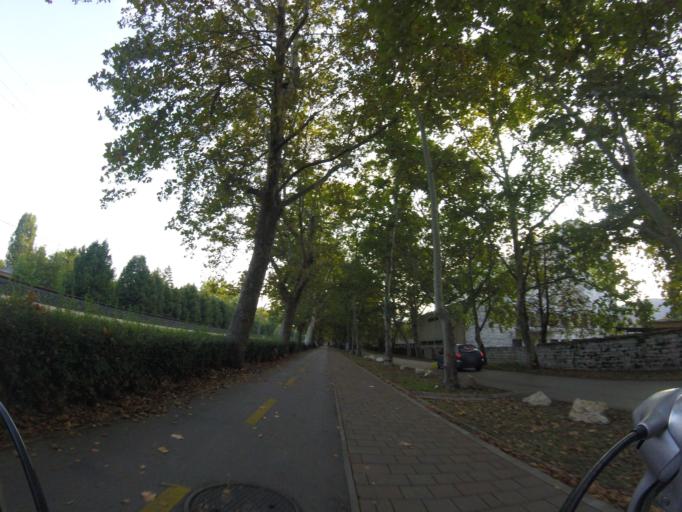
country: HU
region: Somogy
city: Balatonfoldvar
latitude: 46.8555
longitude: 17.8843
